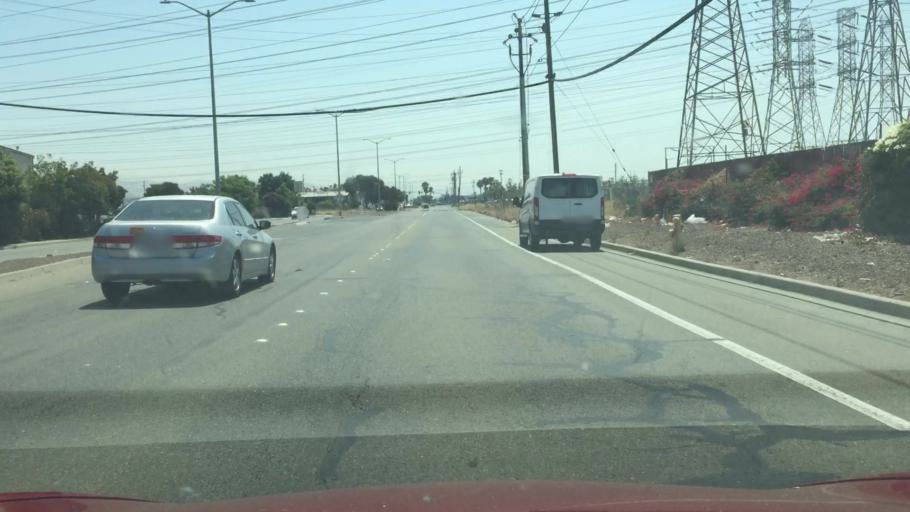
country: US
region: California
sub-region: Alameda County
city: Fremont
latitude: 37.5052
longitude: -121.9833
